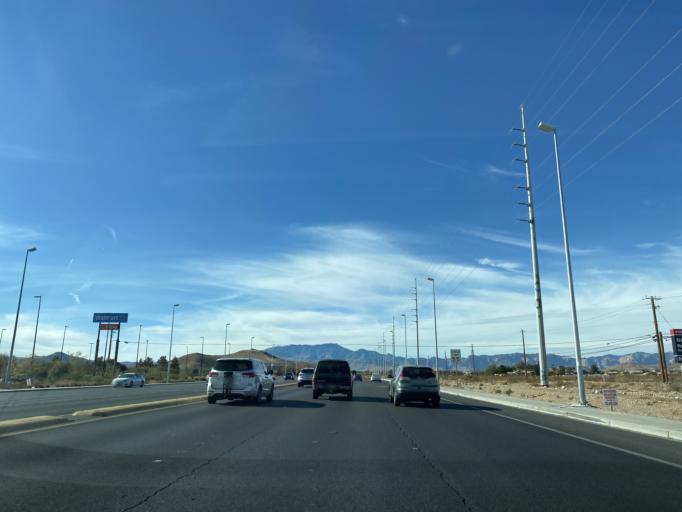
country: US
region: Nevada
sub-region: Clark County
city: Enterprise
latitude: 36.0218
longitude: -115.2443
